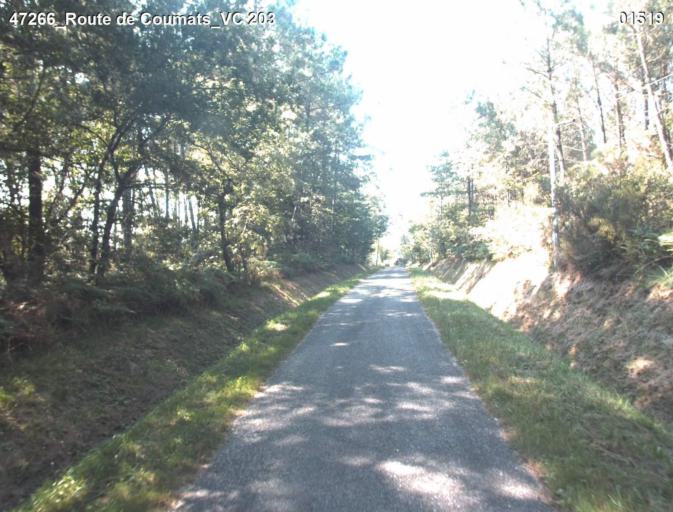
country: FR
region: Aquitaine
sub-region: Departement des Landes
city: Gabarret
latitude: 44.0051
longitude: 0.0944
